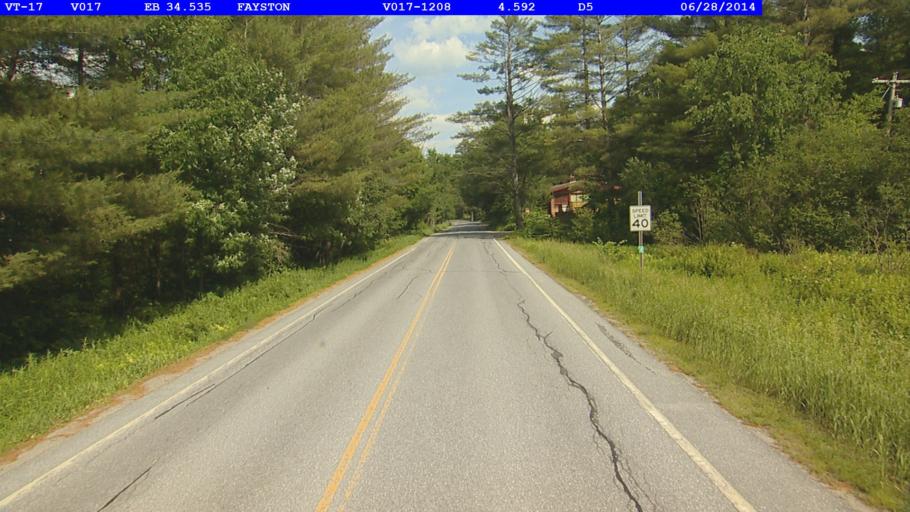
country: US
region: Vermont
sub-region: Washington County
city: Waterbury
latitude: 44.1828
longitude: -72.8669
